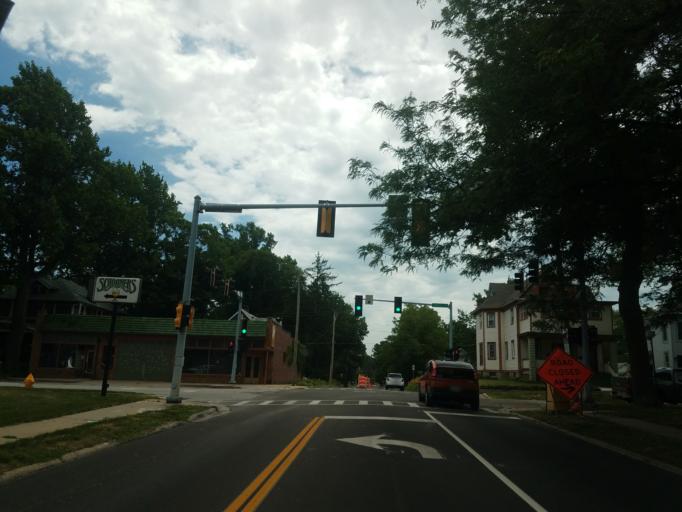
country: US
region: Illinois
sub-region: McLean County
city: Bloomington
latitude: 40.4782
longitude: -88.9846
